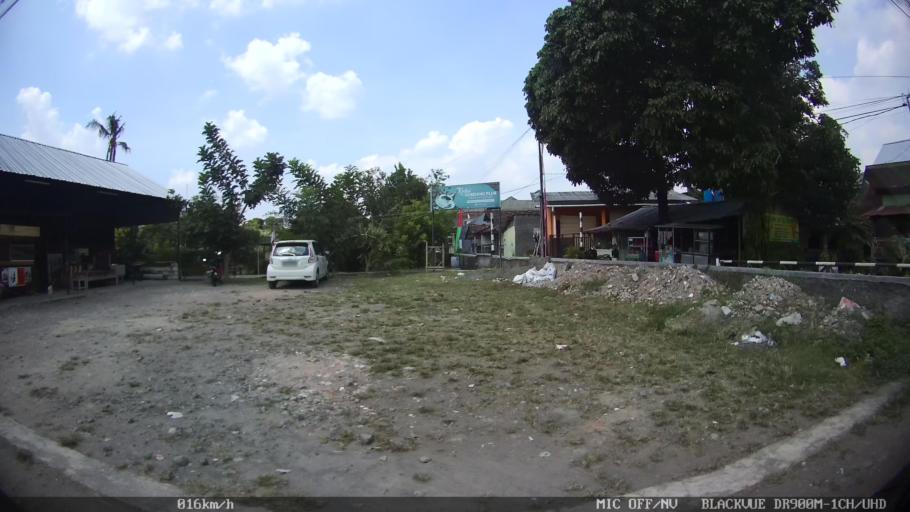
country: ID
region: Daerah Istimewa Yogyakarta
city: Depok
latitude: -7.7968
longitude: 110.4057
